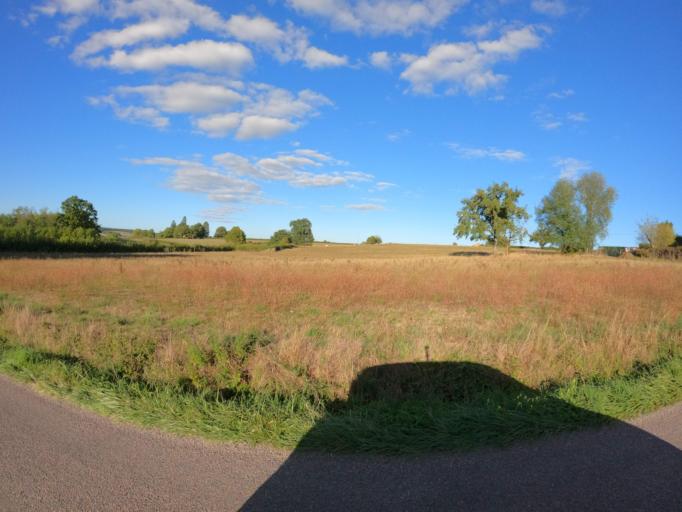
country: FR
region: Bourgogne
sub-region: Departement de Saone-et-Loire
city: Ecuisses
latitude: 46.7528
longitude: 4.5167
